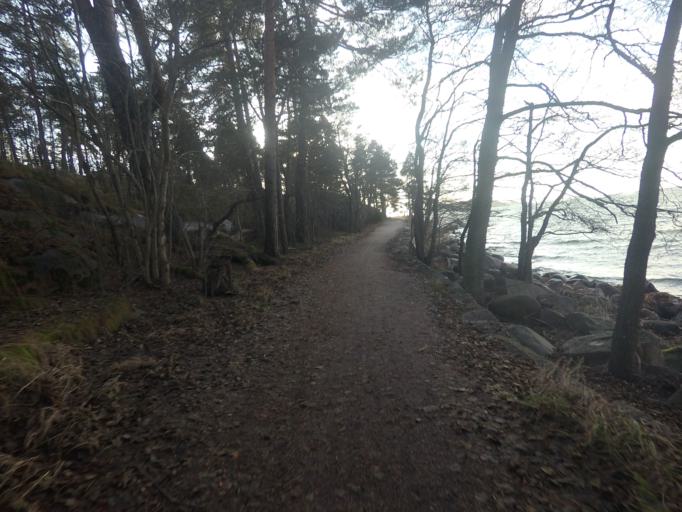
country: FI
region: Uusimaa
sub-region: Helsinki
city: Otaniemi
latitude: 60.1668
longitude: 24.8305
